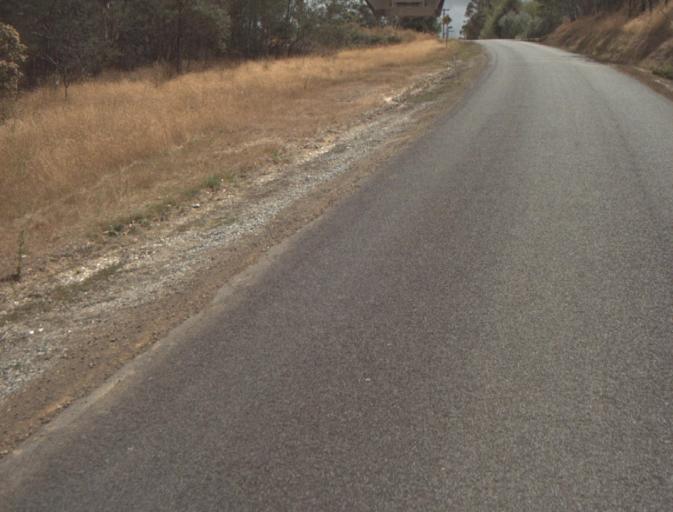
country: AU
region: Tasmania
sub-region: Launceston
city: Mayfield
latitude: -41.2186
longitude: 147.1375
